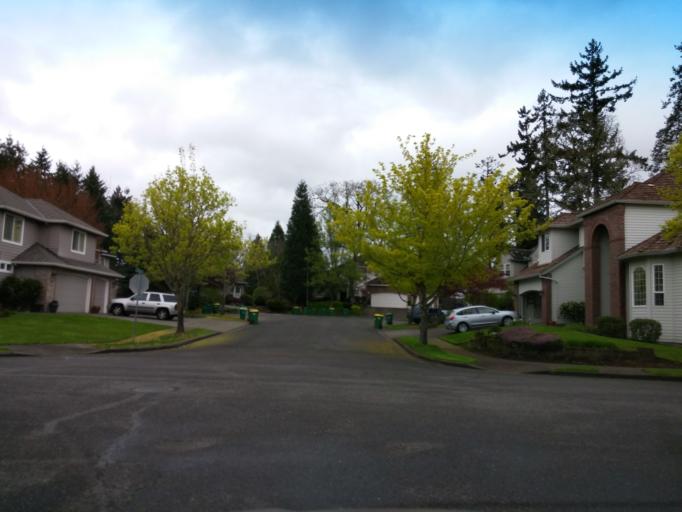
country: US
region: Oregon
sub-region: Washington County
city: Oak Hills
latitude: 45.5176
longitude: -122.8499
